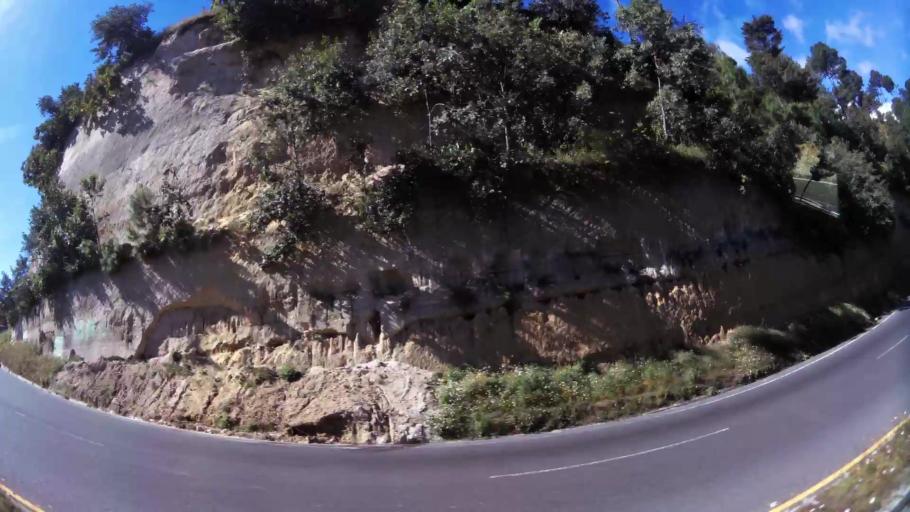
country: GT
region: Solola
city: Nahuala
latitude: 14.8304
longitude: -91.3275
